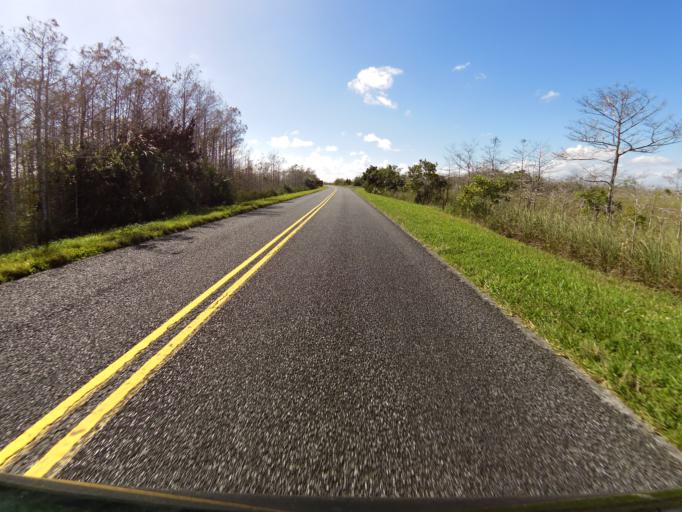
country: US
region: Florida
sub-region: Miami-Dade County
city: Florida City
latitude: 25.4287
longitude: -80.7697
